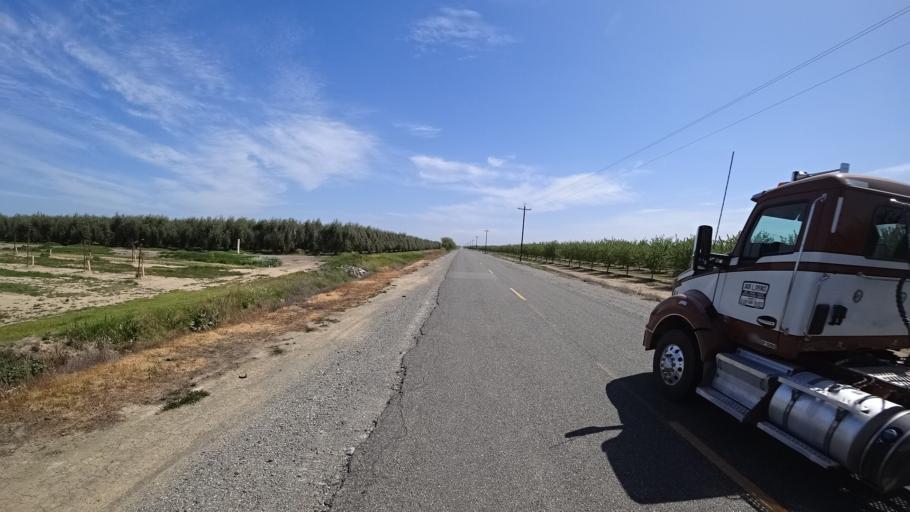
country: US
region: California
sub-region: Glenn County
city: Hamilton City
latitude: 39.6524
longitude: -122.0805
